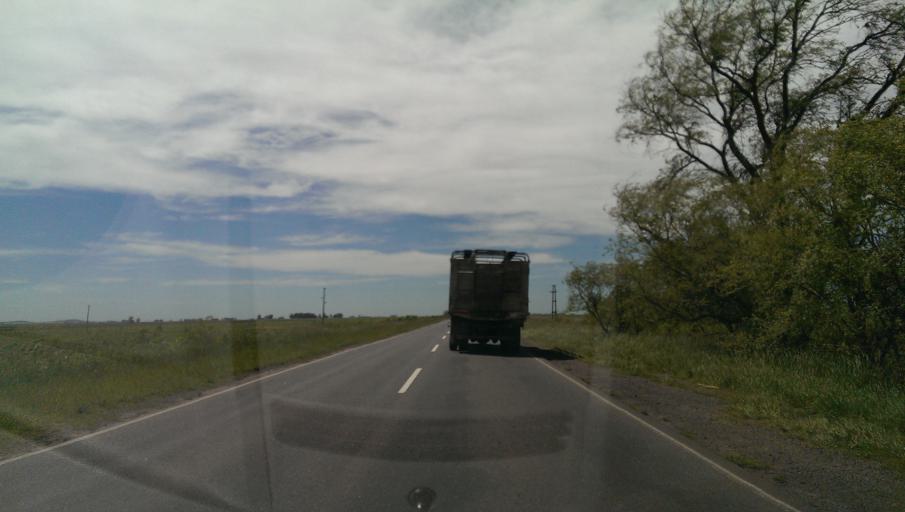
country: AR
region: Buenos Aires
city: Olavarria
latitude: -37.0627
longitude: -60.4616
